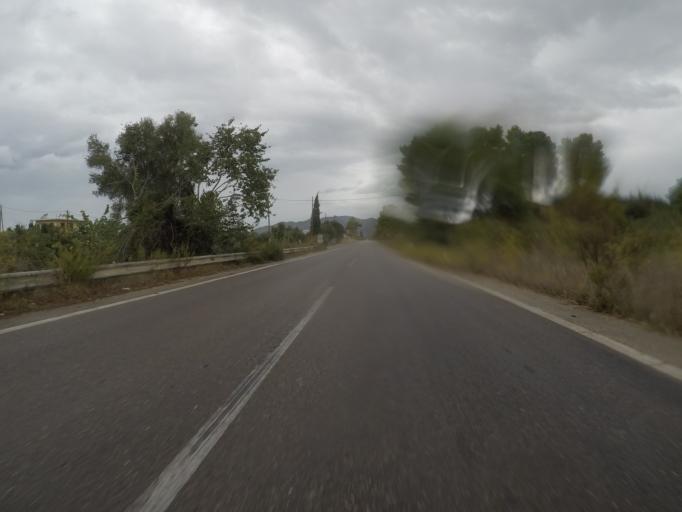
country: GR
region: West Greece
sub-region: Nomos Ileias
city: Zacharo
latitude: 37.4411
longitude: 21.6612
